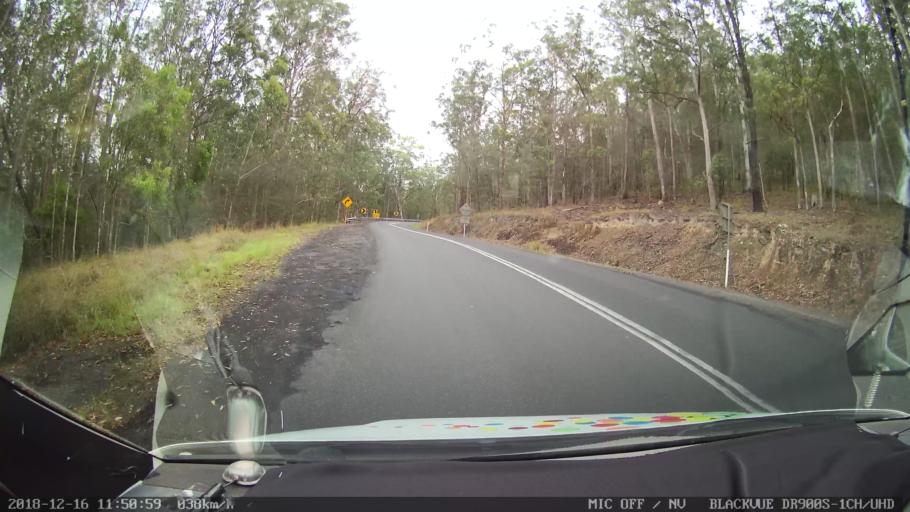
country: AU
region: New South Wales
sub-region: Tenterfield Municipality
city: Carrolls Creek
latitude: -28.9060
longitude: 152.2642
